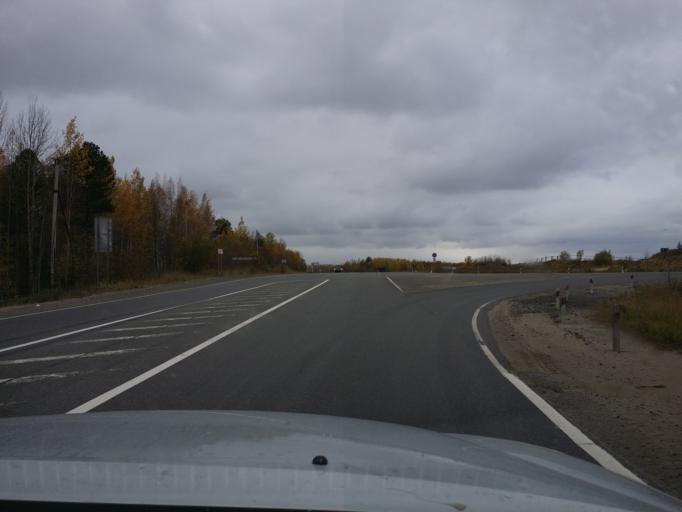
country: RU
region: Khanty-Mansiyskiy Avtonomnyy Okrug
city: Megion
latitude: 61.1106
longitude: 76.0274
